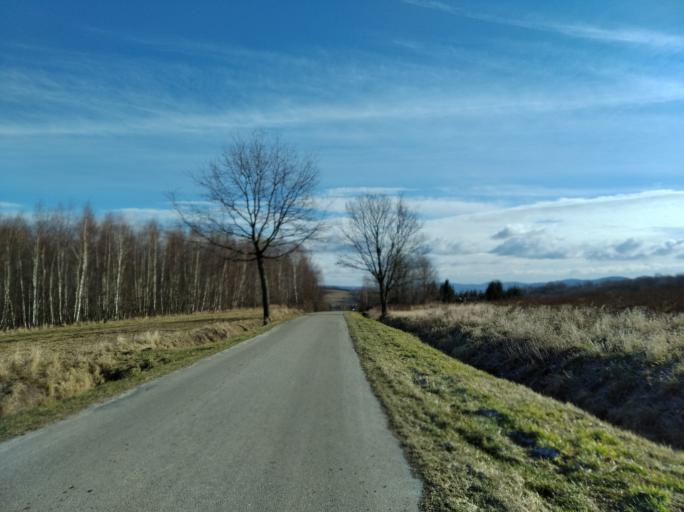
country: PL
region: Subcarpathian Voivodeship
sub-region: Powiat strzyzowski
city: Wisniowa
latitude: 49.9042
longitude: 21.6543
